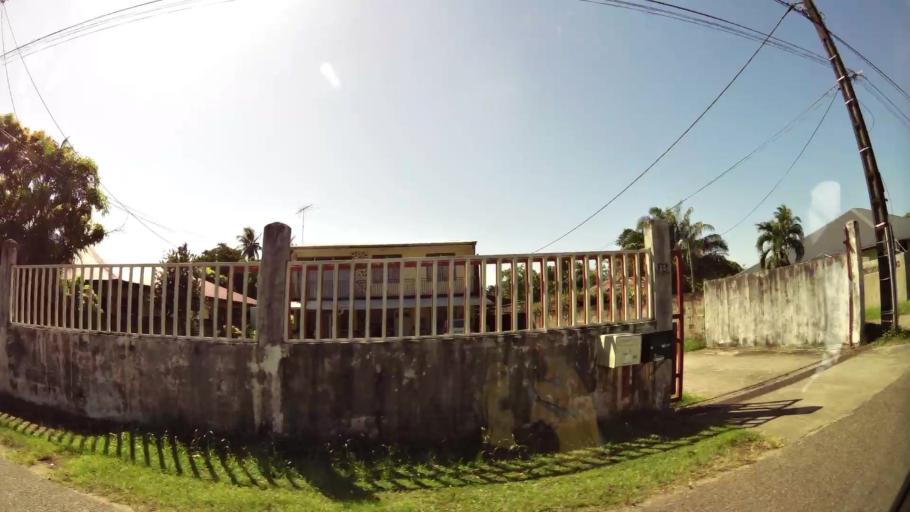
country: GF
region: Guyane
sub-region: Guyane
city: Remire-Montjoly
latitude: 4.9129
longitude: -52.2685
